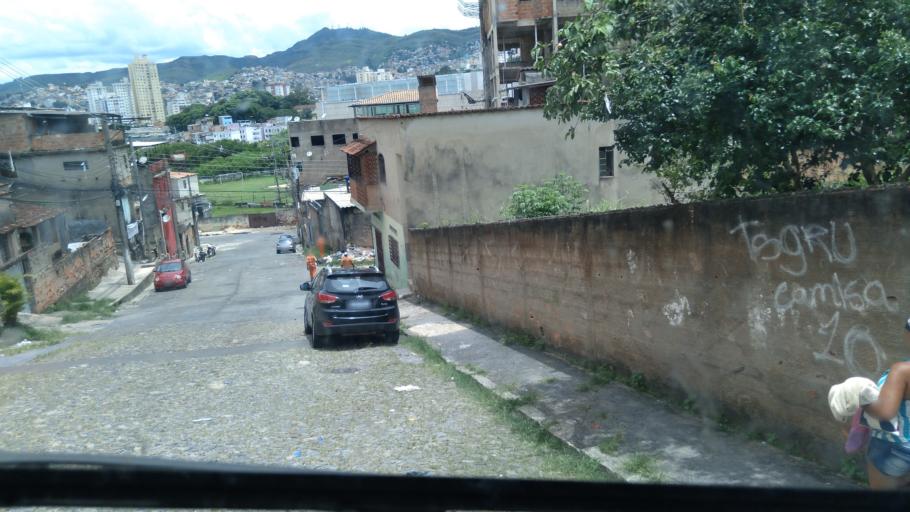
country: BR
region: Minas Gerais
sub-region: Belo Horizonte
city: Belo Horizonte
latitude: -19.9179
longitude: -43.9220
